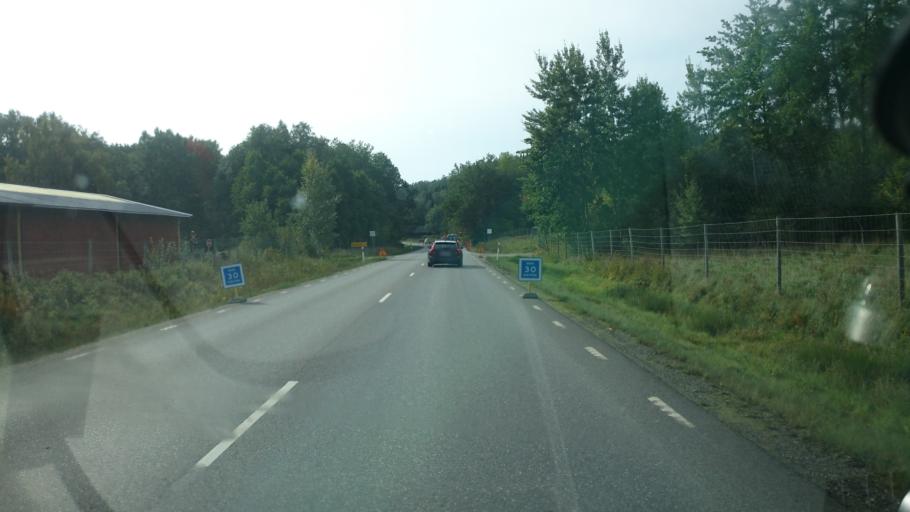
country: SE
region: Vaestra Goetaland
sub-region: Alingsas Kommun
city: Alingsas
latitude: 57.9870
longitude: 12.4395
